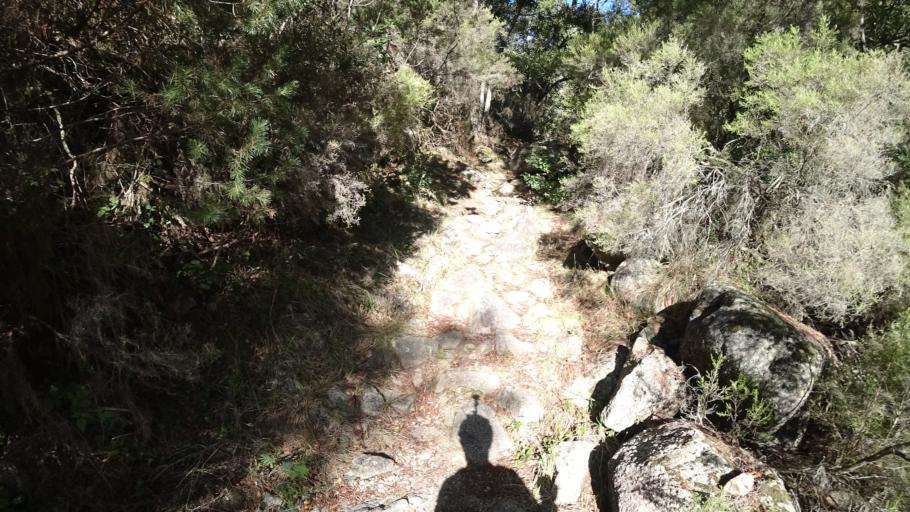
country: PT
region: Braga
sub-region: Vieira do Minho
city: Real
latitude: 41.7591
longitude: -8.1496
